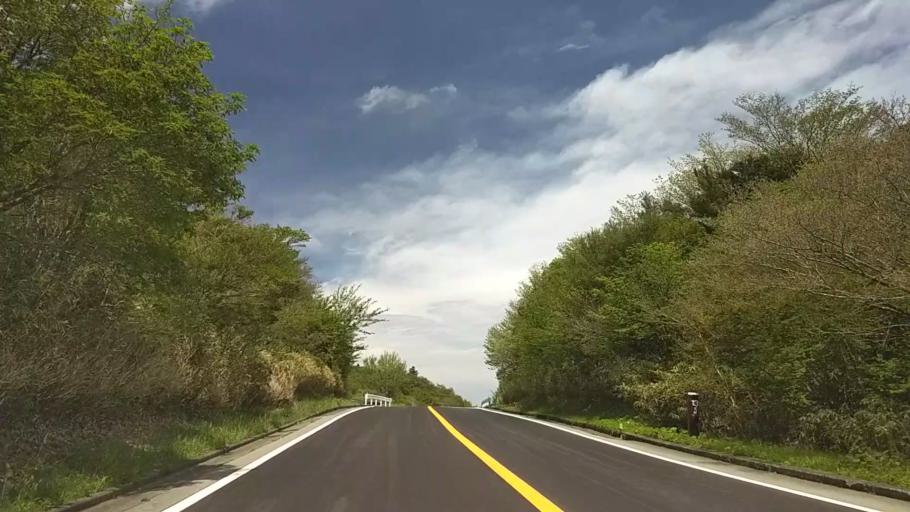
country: JP
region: Kanagawa
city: Hakone
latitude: 35.1882
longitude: 139.0544
